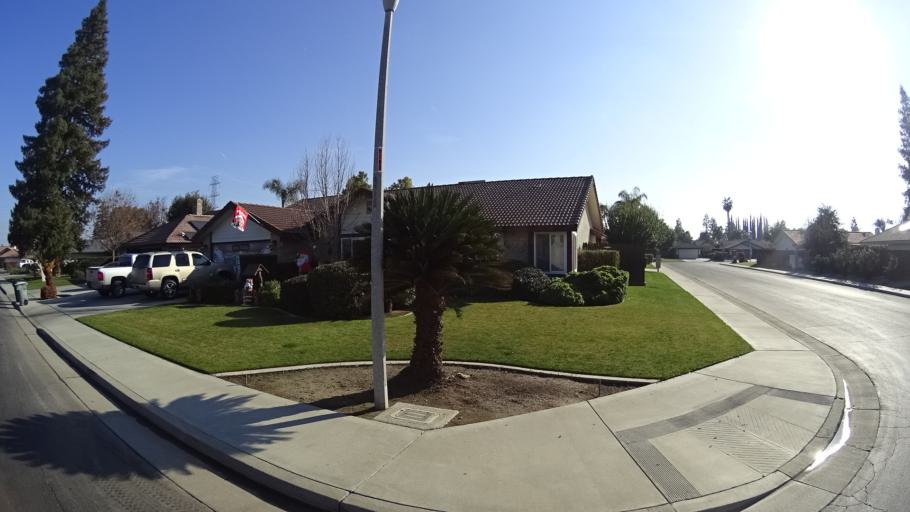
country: US
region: California
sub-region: Kern County
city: Greenacres
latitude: 35.3284
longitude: -119.0987
